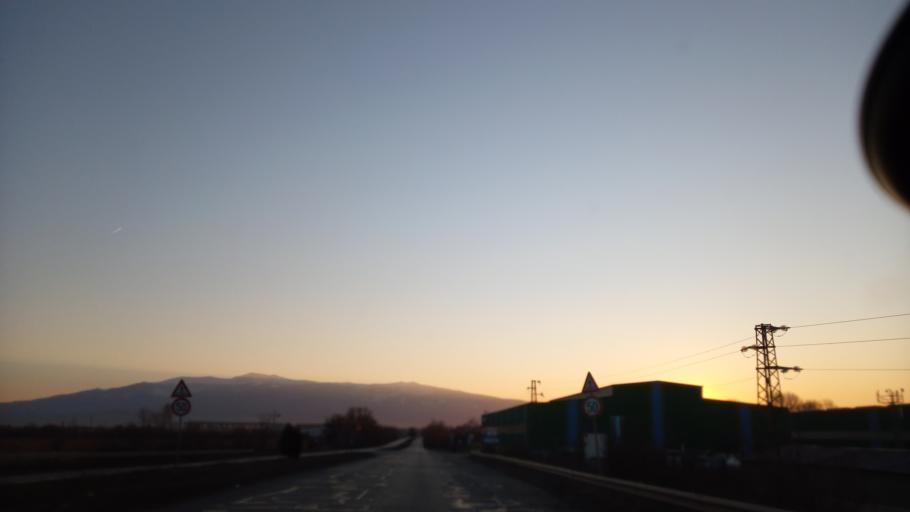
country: BG
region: Sofia-Capital
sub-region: Stolichna Obshtina
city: Sofia
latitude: 42.7197
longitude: 23.4442
